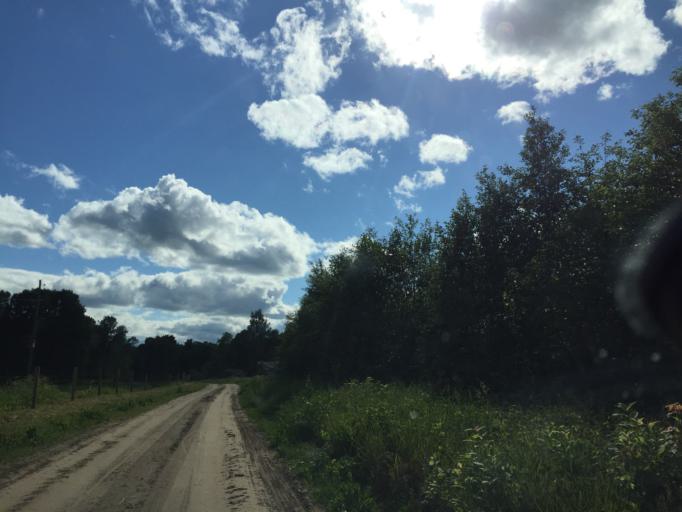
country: LV
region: Vecumnieki
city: Vecumnieki
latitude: 56.4251
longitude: 24.6175
